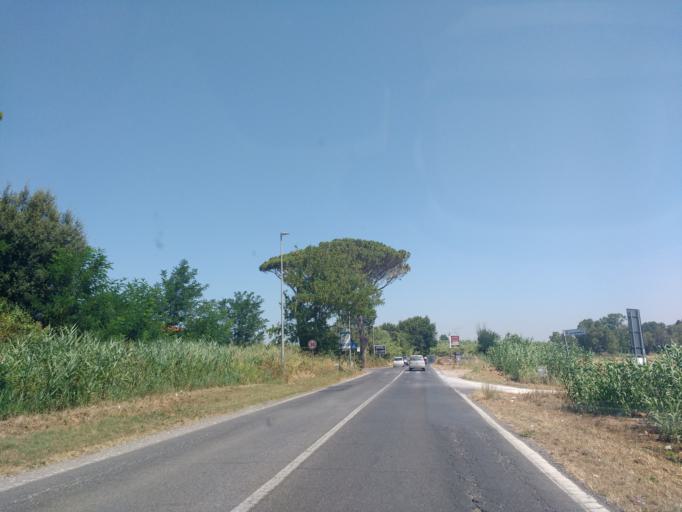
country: IT
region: Latium
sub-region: Citta metropolitana di Roma Capitale
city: Maccarese
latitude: 41.8721
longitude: 12.2089
